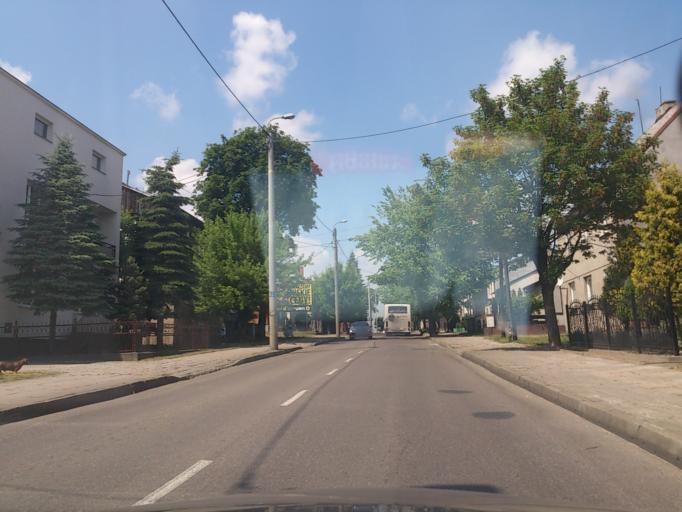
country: PL
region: Kujawsko-Pomorskie
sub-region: Powiat rypinski
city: Rypin
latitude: 53.0705
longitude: 19.4021
